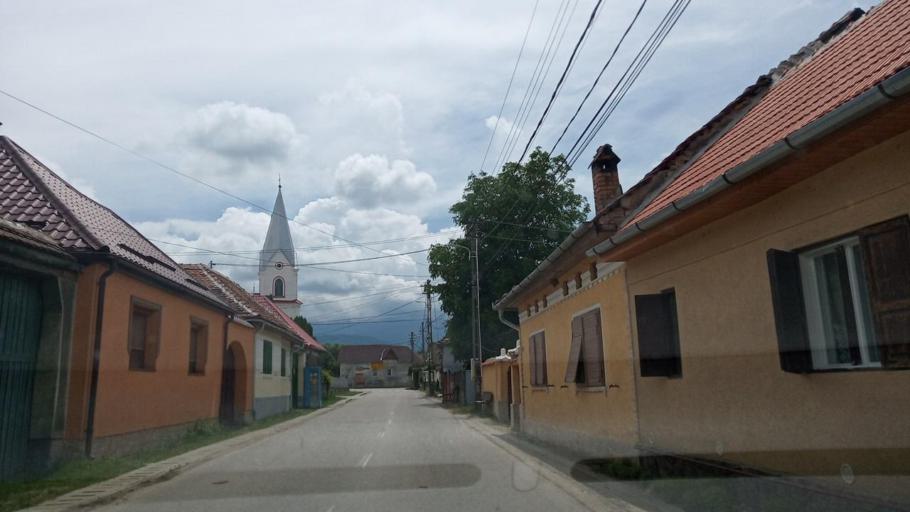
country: RO
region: Sibiu
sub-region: Comuna Porumbacu de Jos
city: Porumbacu de Jos
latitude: 45.7167
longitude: 24.4740
